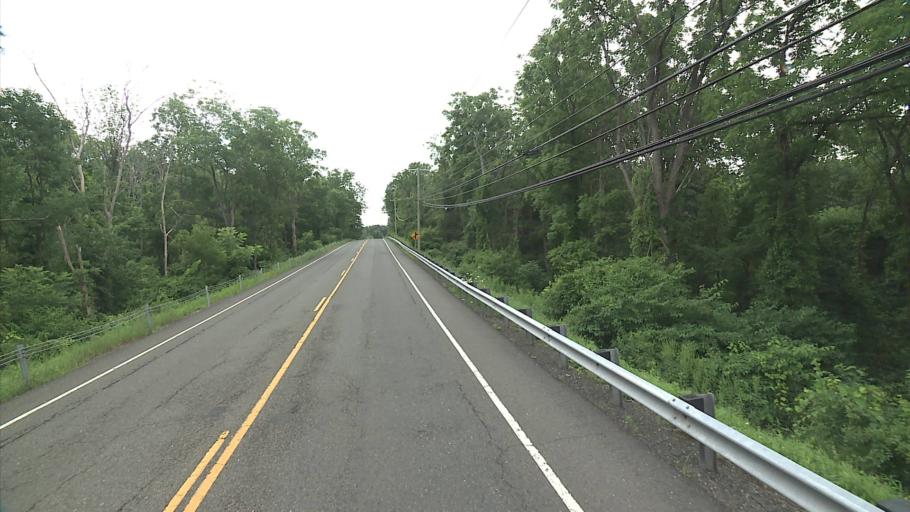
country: US
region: Connecticut
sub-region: Litchfield County
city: New Milford
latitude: 41.5515
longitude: -73.3818
